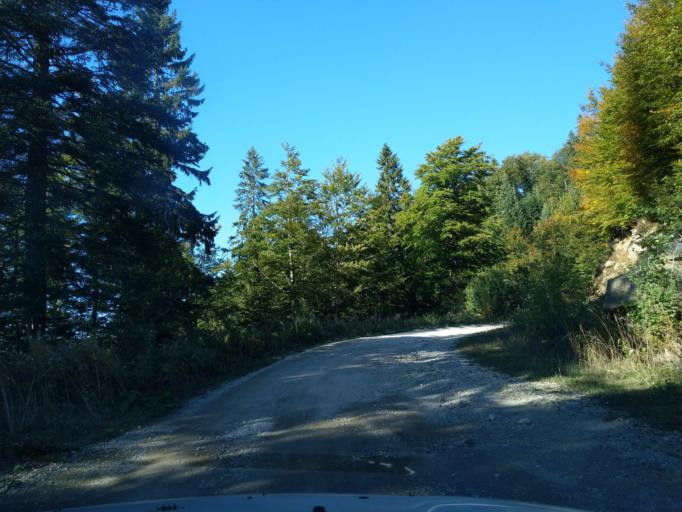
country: RS
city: Sokolovica
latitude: 43.3658
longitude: 20.2590
